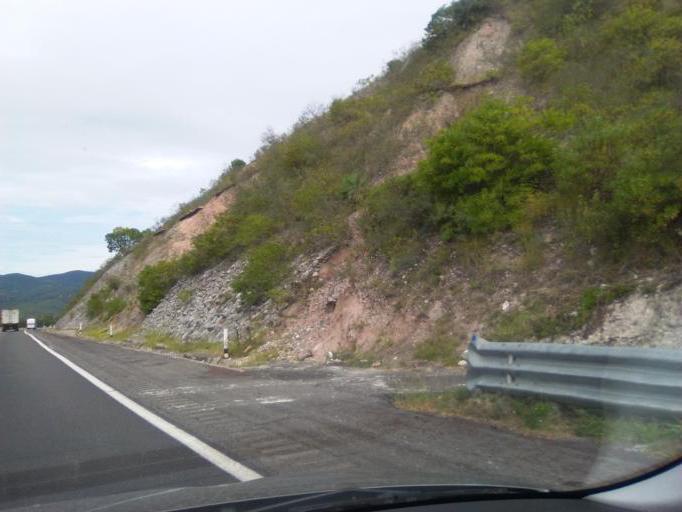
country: MX
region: Guerrero
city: Zumpango del Rio
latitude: 17.6214
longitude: -99.5172
